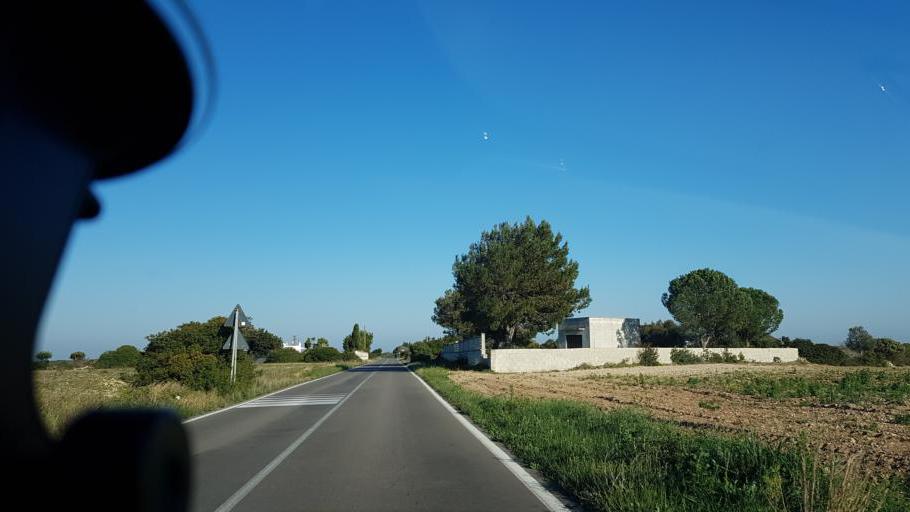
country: IT
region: Apulia
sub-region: Provincia di Lecce
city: Struda
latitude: 40.3939
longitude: 18.2729
